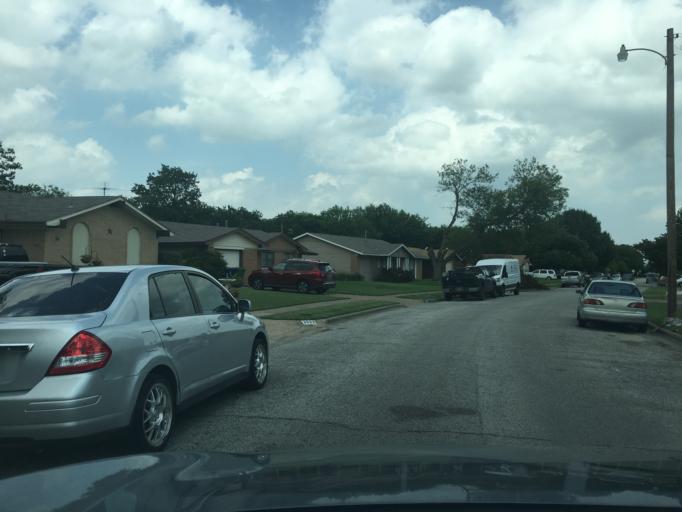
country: US
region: Texas
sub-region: Dallas County
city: Garland
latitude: 32.9140
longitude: -96.6864
